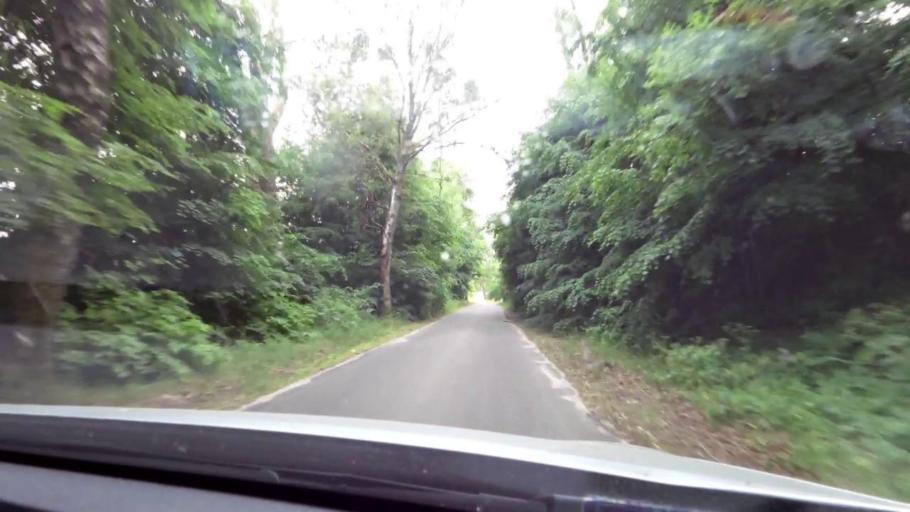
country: PL
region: Pomeranian Voivodeship
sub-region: Powiat bytowski
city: Trzebielino
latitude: 54.2525
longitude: 17.0045
